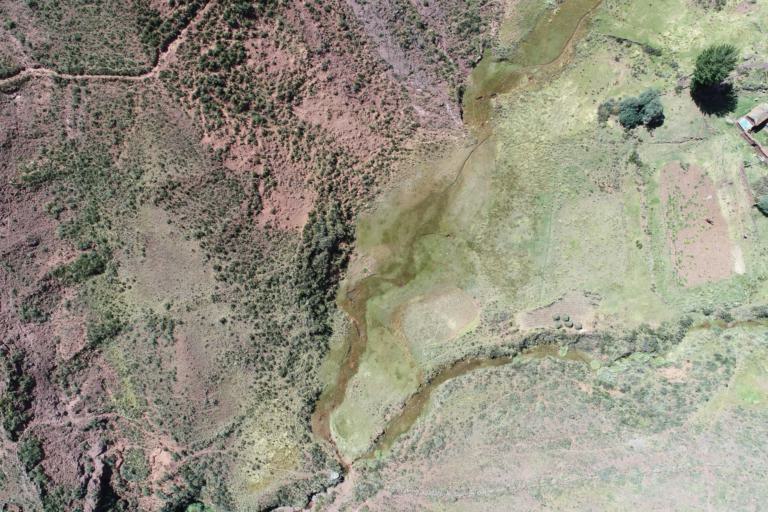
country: BO
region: La Paz
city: Tiahuanaco
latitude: -16.6063
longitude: -68.7610
